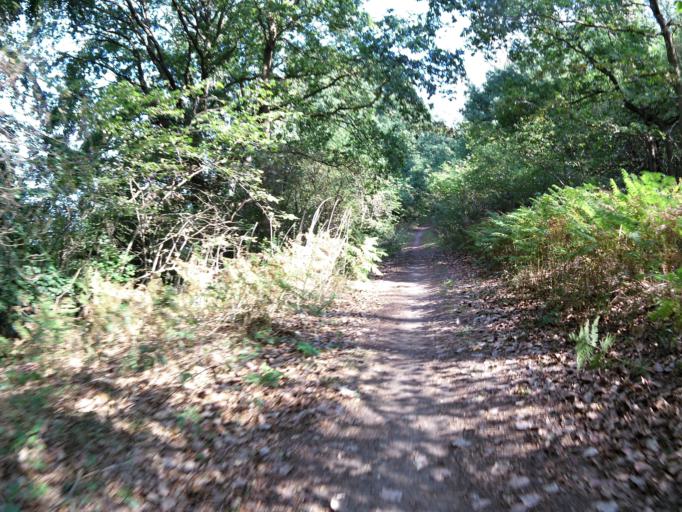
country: DE
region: Mecklenburg-Vorpommern
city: Loddin
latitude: 53.9555
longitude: 14.0390
